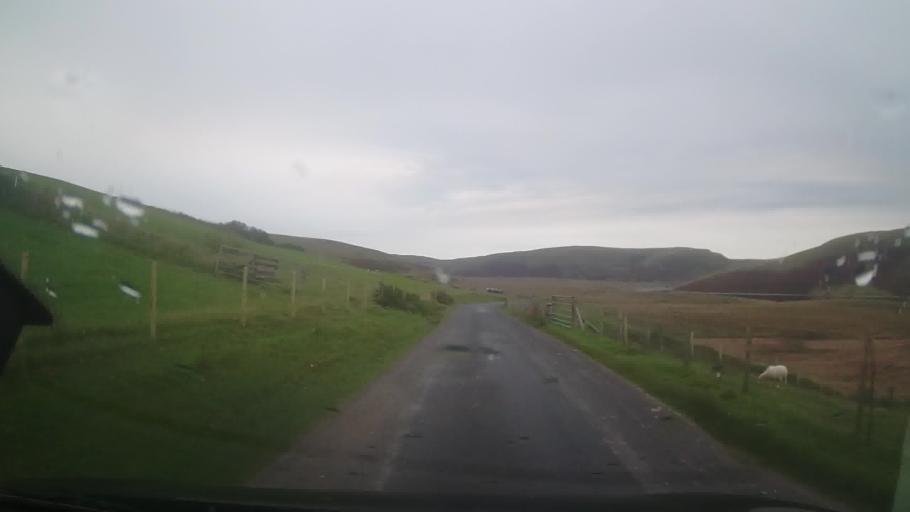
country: GB
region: Wales
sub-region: Sir Powys
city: Rhayader
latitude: 52.3177
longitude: -3.6304
